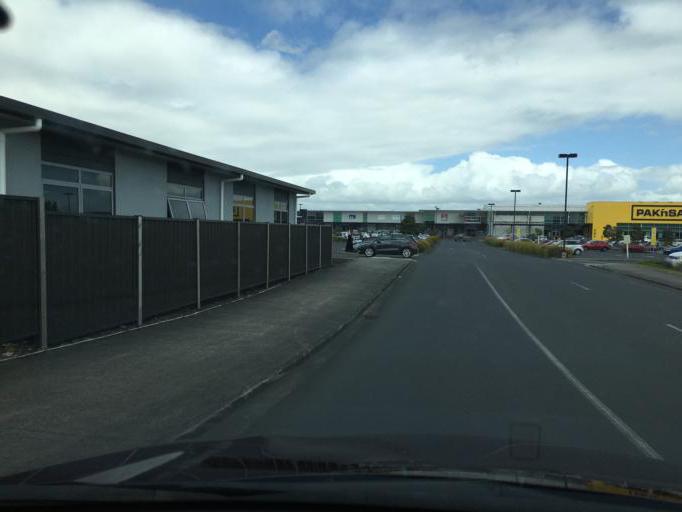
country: NZ
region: Waikato
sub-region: Waipa District
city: Cambridge
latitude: -38.0066
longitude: 175.3399
